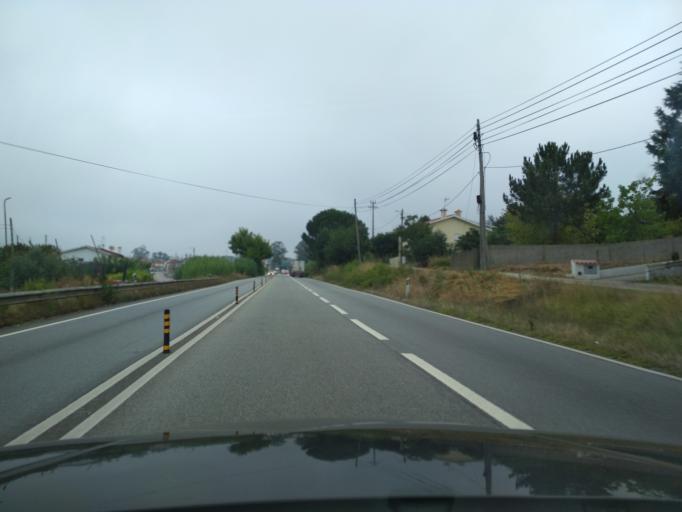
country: PT
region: Aveiro
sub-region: Mealhada
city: Pampilhosa do Botao
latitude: 40.2852
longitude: -8.4458
